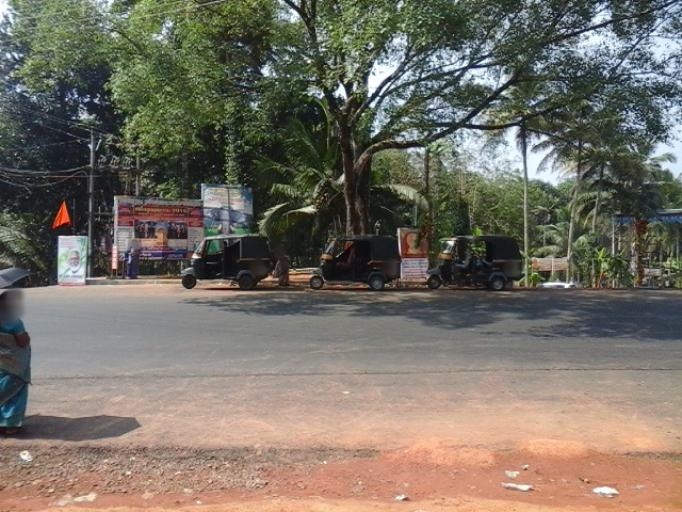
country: IN
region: Kerala
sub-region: Kottayam
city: Erattupetta
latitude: 9.5943
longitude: 76.7322
